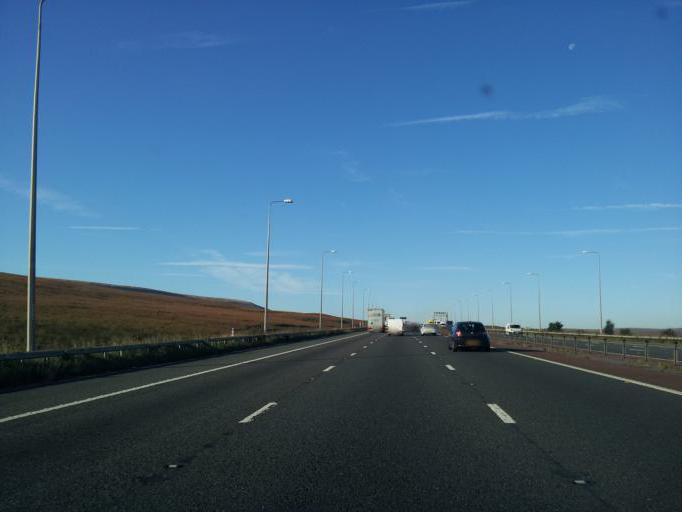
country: GB
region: England
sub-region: Calderdale
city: Ripponden
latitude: 53.6380
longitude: -1.9743
